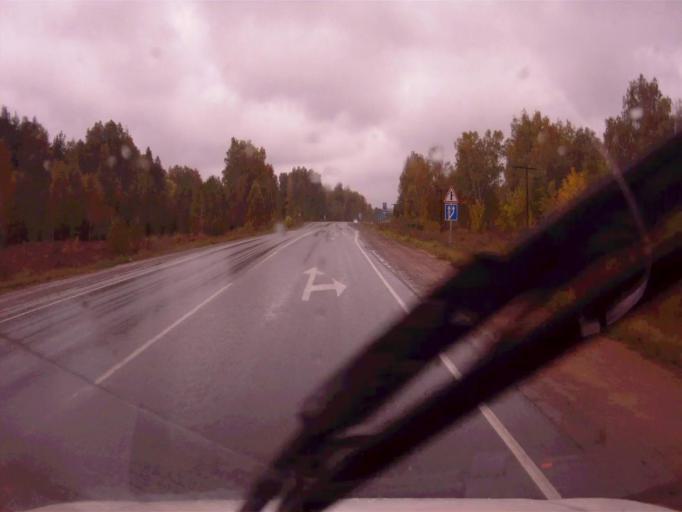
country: RU
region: Chelyabinsk
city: Argayash
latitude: 55.4700
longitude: 60.9039
